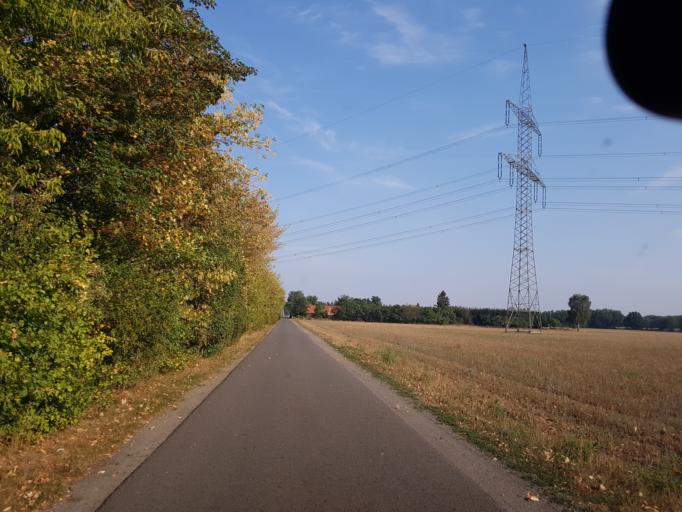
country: DE
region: Brandenburg
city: Finsterwalde
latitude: 51.6537
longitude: 13.7219
